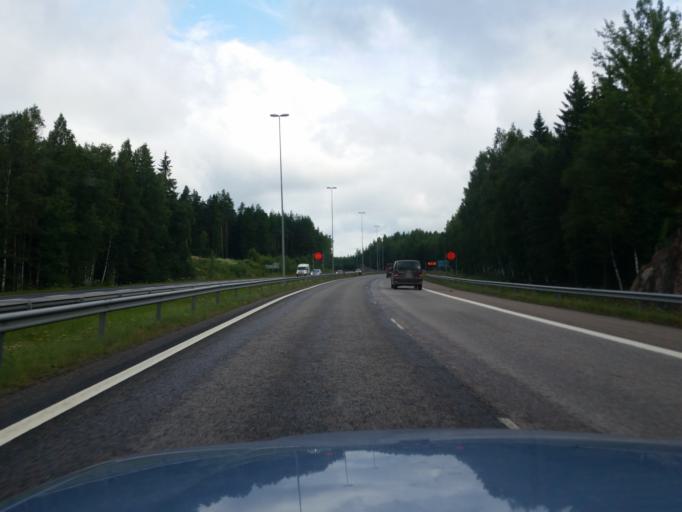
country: FI
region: Uusimaa
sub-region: Helsinki
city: Kirkkonummi
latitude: 60.2757
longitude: 24.4511
